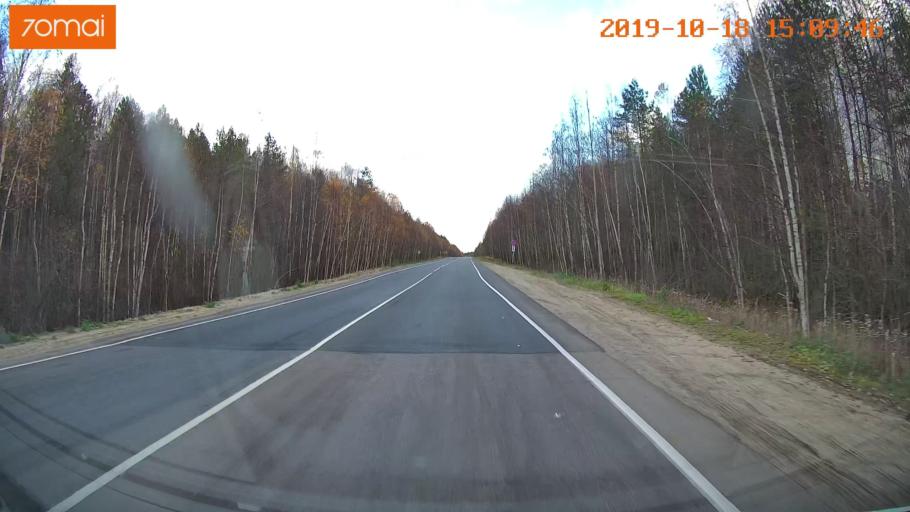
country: RU
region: Vladimir
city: Gus'-Khrustal'nyy
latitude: 55.5674
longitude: 40.6262
